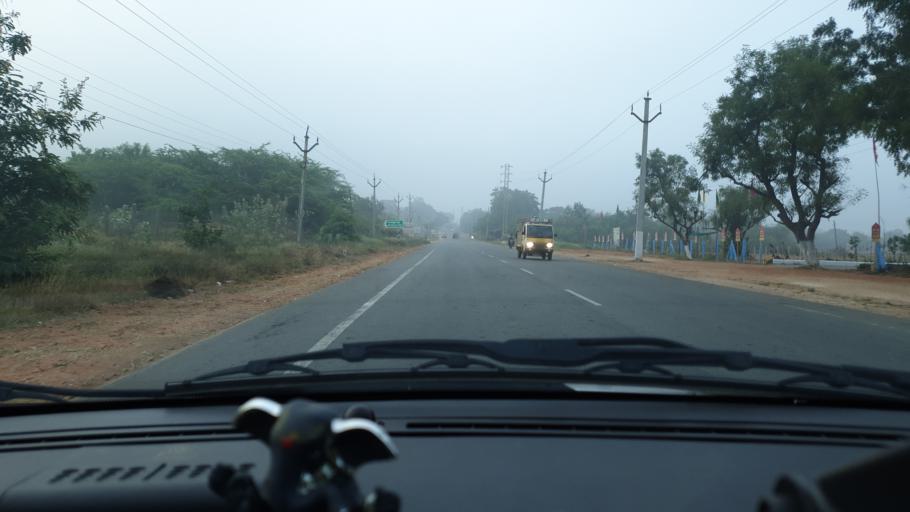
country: IN
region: Telangana
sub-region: Mahbubnagar
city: Farrukhnagar
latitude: 16.8745
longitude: 78.5293
